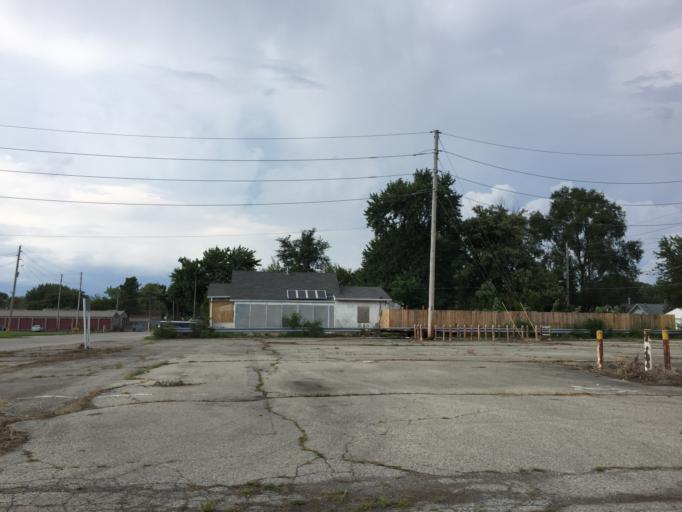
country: US
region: Indiana
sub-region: Howard County
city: Kokomo
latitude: 40.4699
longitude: -86.1231
